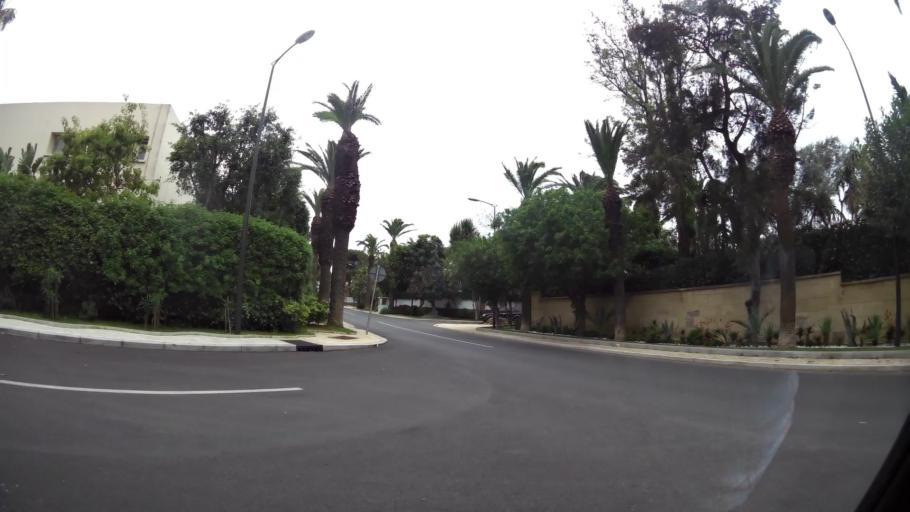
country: MA
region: Grand Casablanca
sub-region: Casablanca
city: Casablanca
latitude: 33.5849
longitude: -7.6643
